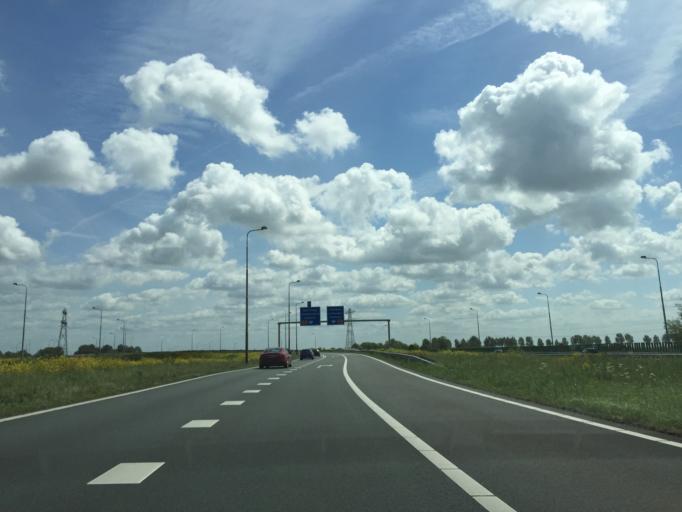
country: NL
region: North Holland
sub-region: Gemeente Haarlem
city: Haarlem
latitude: 52.3708
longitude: 4.6915
